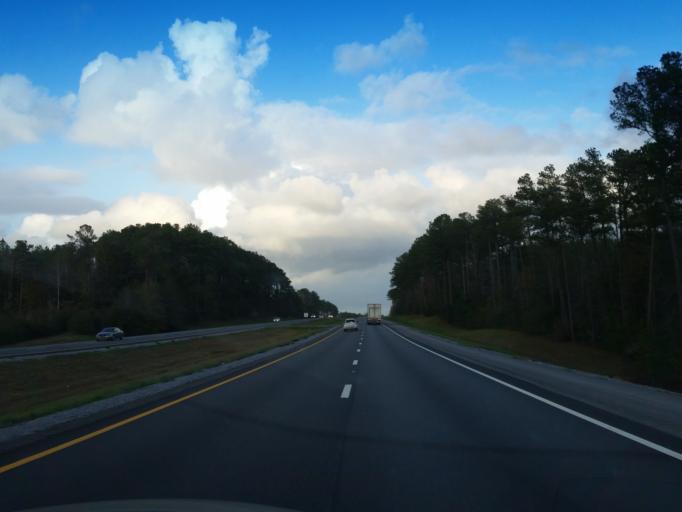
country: US
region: Mississippi
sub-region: Jones County
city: Sharon
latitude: 31.8916
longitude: -89.0330
